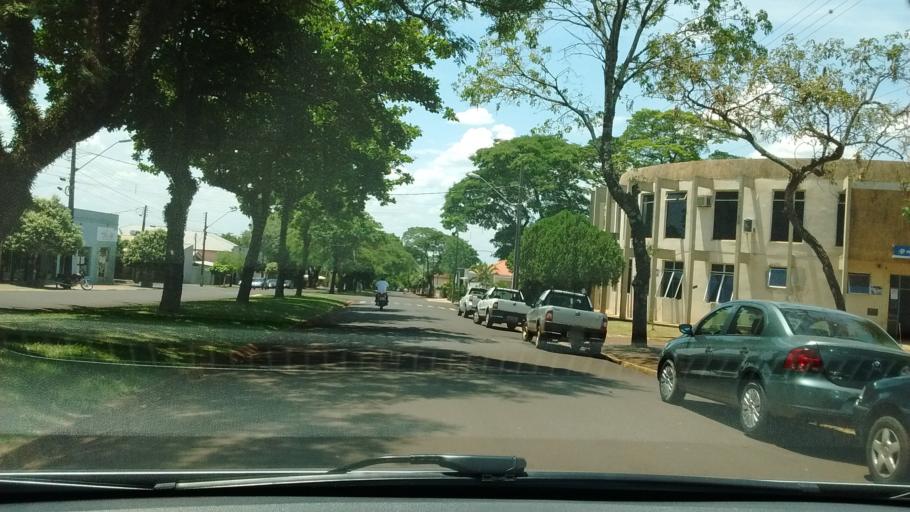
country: BR
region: Parana
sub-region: Corbelia
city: Corbelia
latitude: -24.5379
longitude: -52.9904
